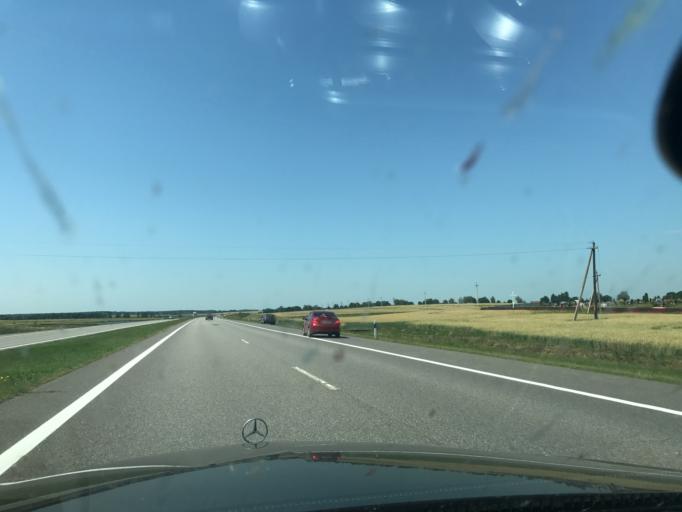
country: BY
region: Minsk
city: Stan'kava
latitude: 53.6769
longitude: 27.2593
